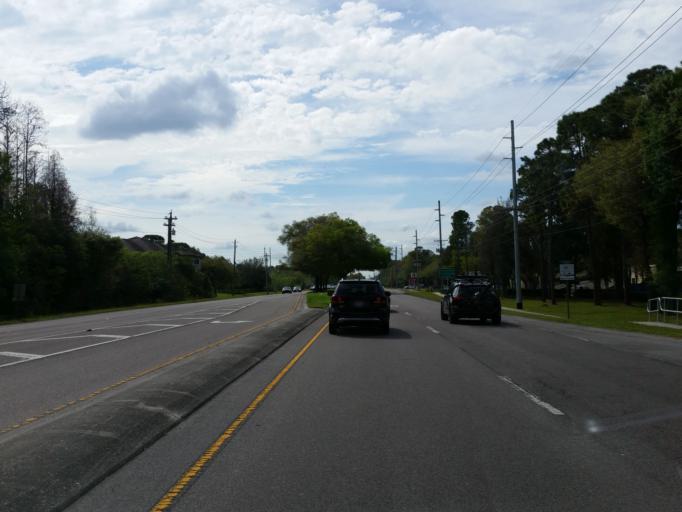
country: US
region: Florida
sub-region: Hillsborough County
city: Temple Terrace
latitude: 28.0693
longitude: -82.3652
